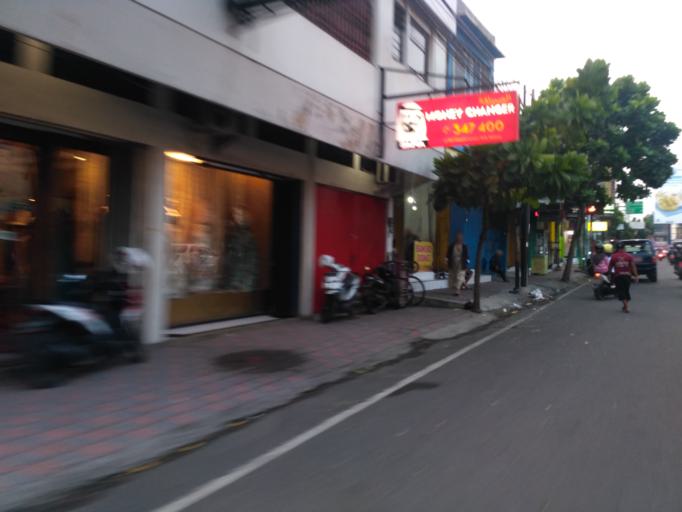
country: ID
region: East Java
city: Malang
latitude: -7.9821
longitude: 112.6271
